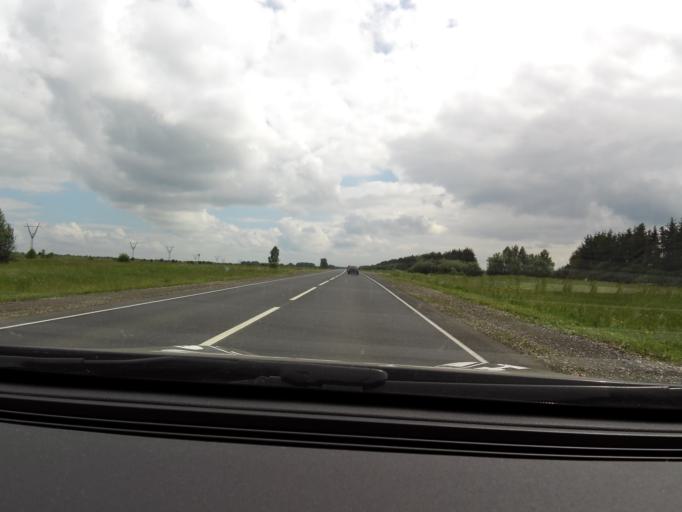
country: RU
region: Perm
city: Orda
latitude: 57.2470
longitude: 57.0459
